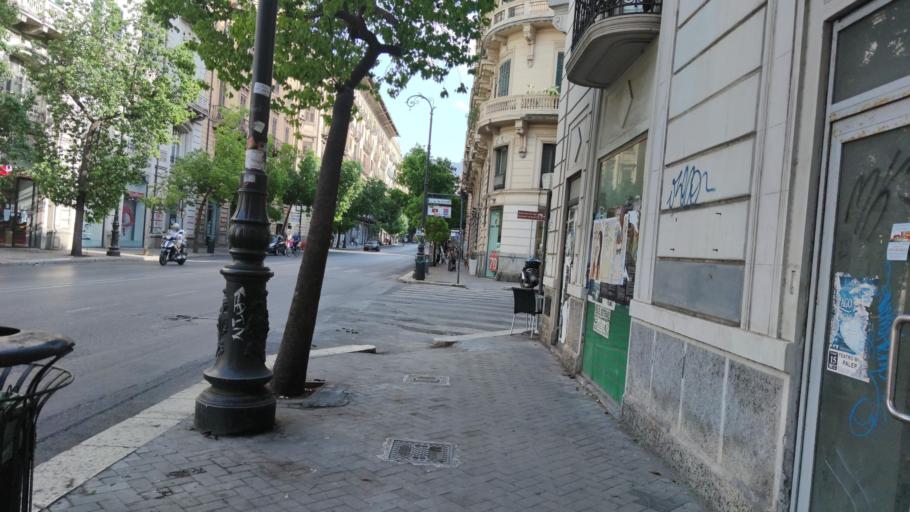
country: IT
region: Sicily
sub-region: Palermo
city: Palermo
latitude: 38.1151
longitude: 13.3643
